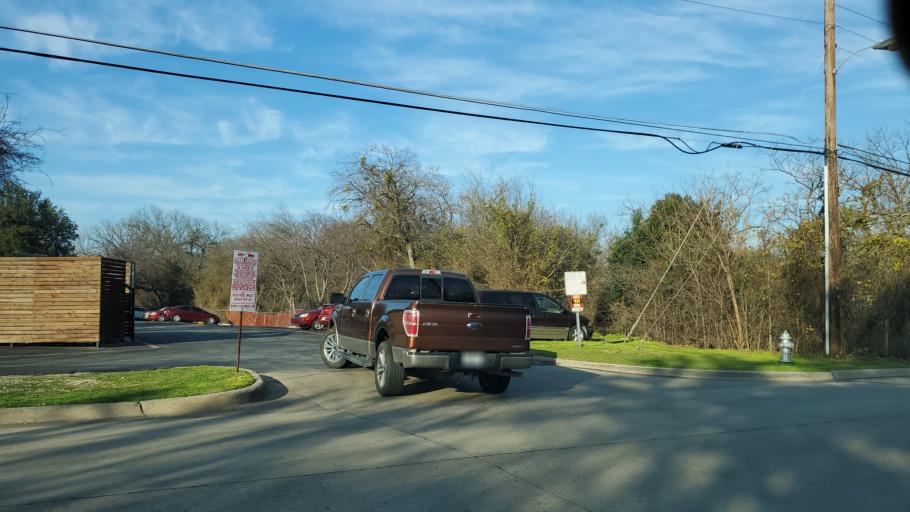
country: US
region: Texas
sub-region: Collin County
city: Plano
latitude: 33.0214
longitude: -96.7131
